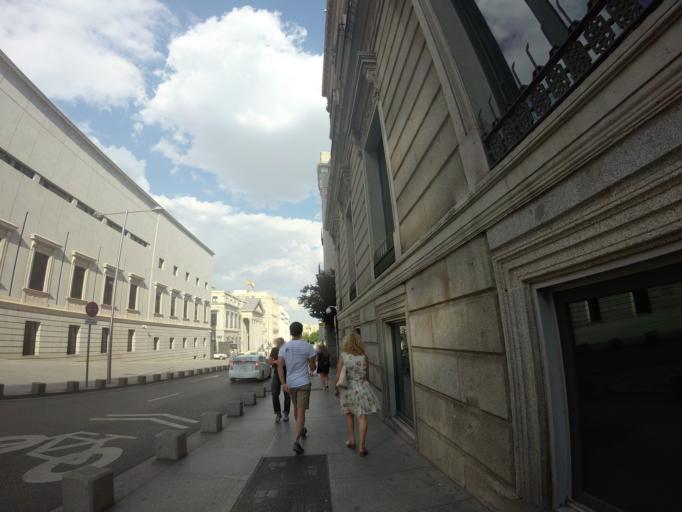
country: ES
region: Madrid
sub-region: Provincia de Madrid
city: Madrid
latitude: 40.4165
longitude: -3.6980
